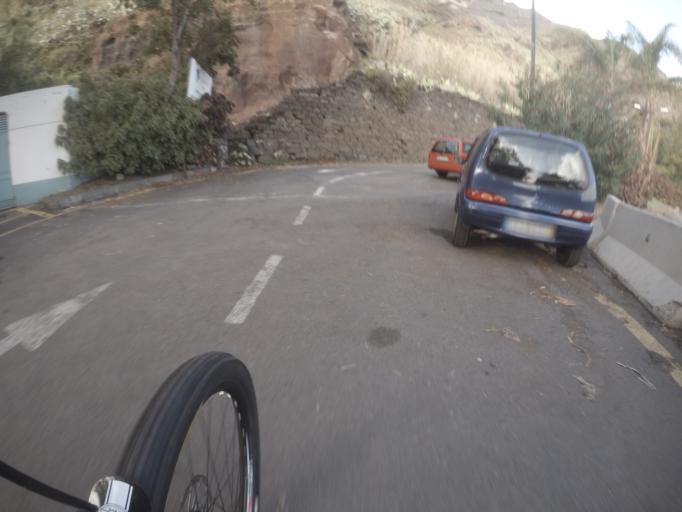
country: PT
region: Madeira
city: Camara de Lobos
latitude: 32.6425
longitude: -16.9554
